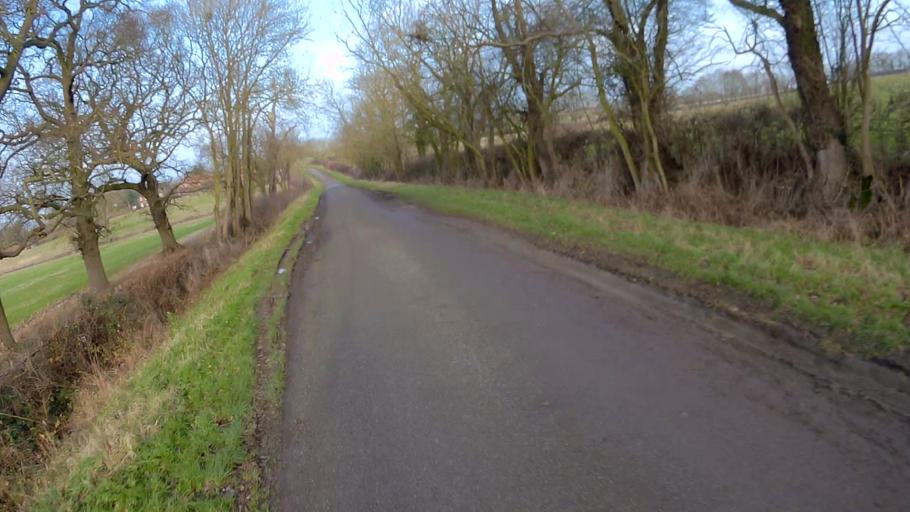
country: GB
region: England
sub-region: Lincolnshire
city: Bourne
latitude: 52.7480
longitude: -0.4173
